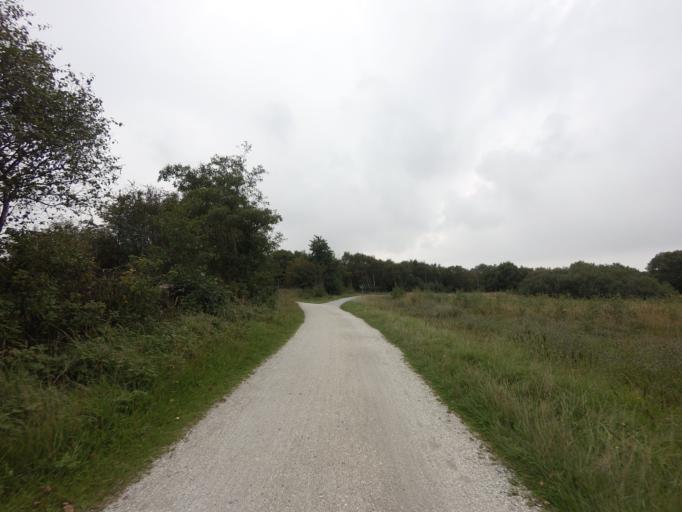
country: NL
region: Friesland
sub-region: Gemeente Schiermonnikoog
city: Schiermonnikoog
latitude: 53.4868
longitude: 6.1598
